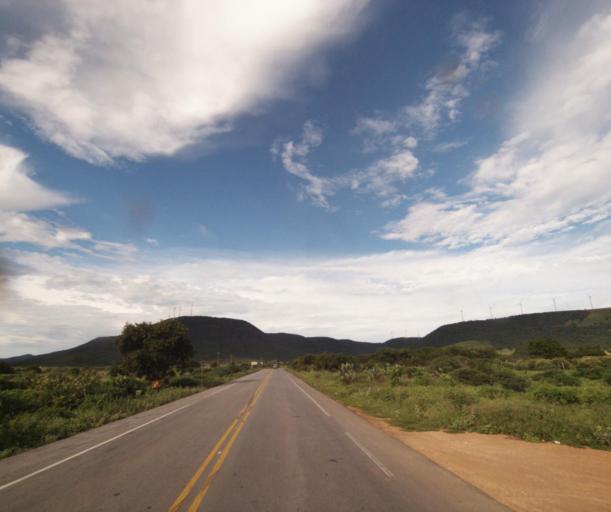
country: BR
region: Bahia
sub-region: Guanambi
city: Guanambi
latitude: -14.1661
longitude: -42.7214
